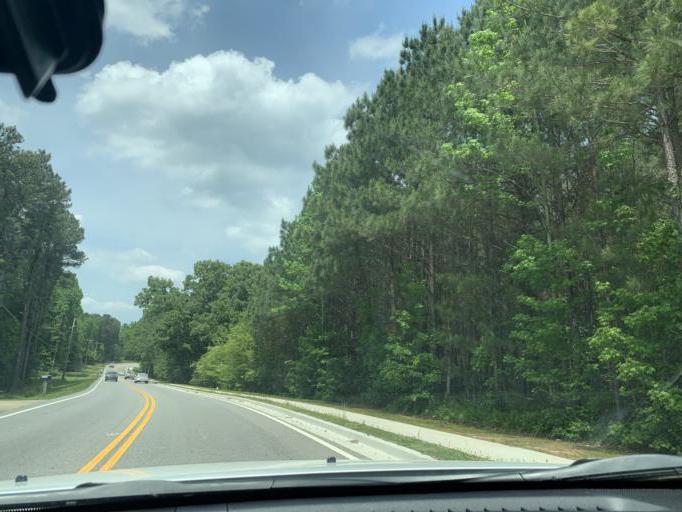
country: US
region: Georgia
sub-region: Forsyth County
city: Cumming
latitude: 34.1308
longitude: -84.1489
